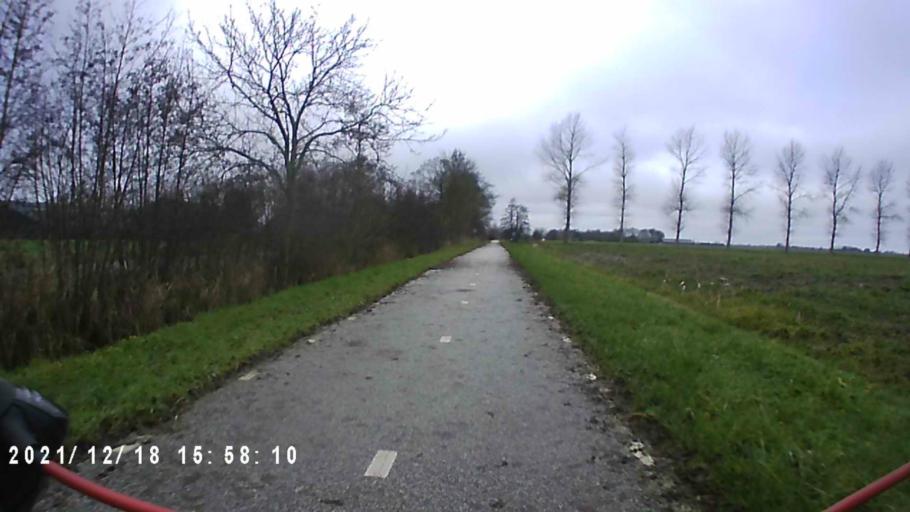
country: NL
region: Friesland
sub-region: Gemeente Dongeradeel
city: Anjum
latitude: 53.3364
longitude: 6.0933
